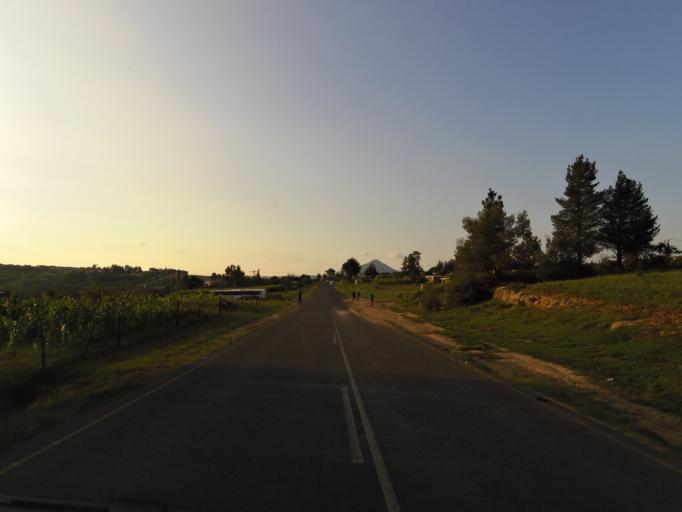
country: LS
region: Leribe
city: Leribe
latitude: -28.9424
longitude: 28.1691
